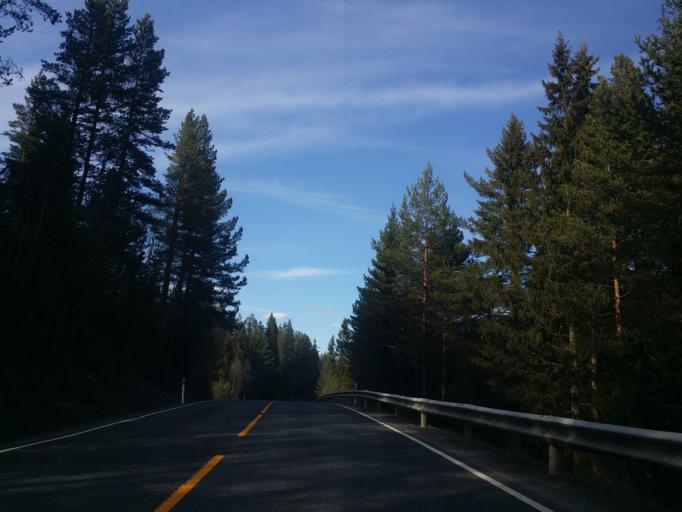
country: NO
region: Buskerud
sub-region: Kongsberg
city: Kongsberg
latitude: 59.6153
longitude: 9.4654
